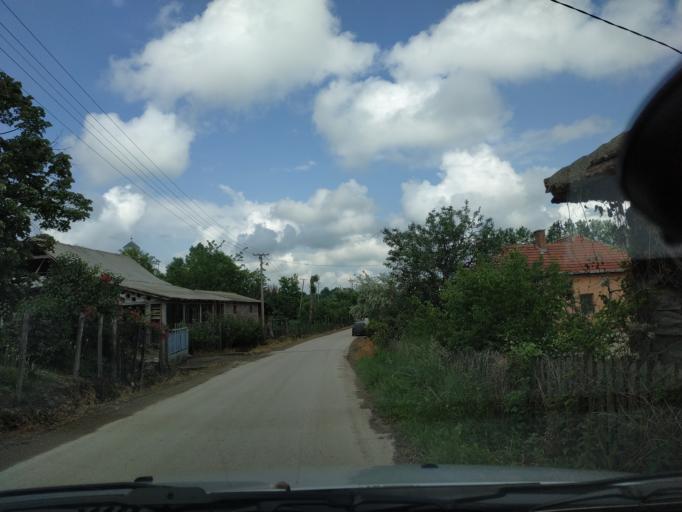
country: RS
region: Central Serbia
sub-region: Nisavski Okrug
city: Aleksinac
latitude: 43.4276
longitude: 21.5853
